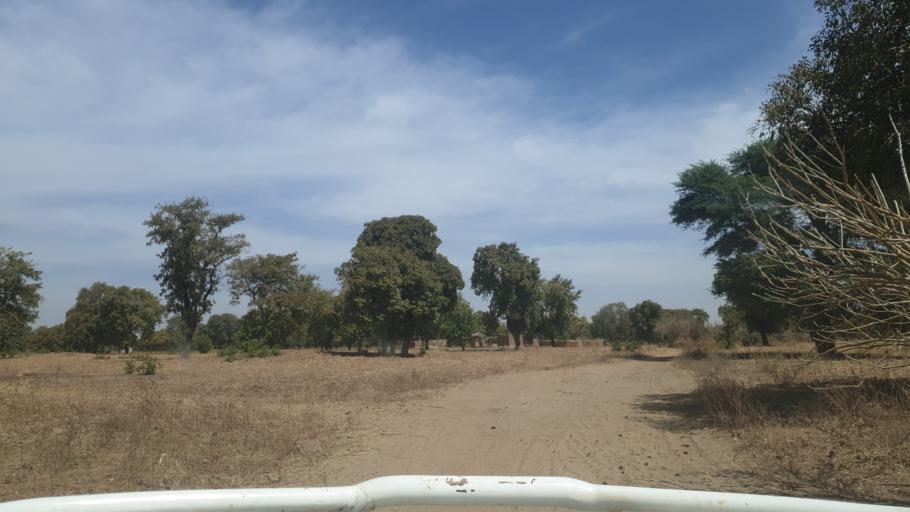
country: ML
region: Sikasso
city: Yorosso
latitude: 12.2905
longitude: -4.6688
